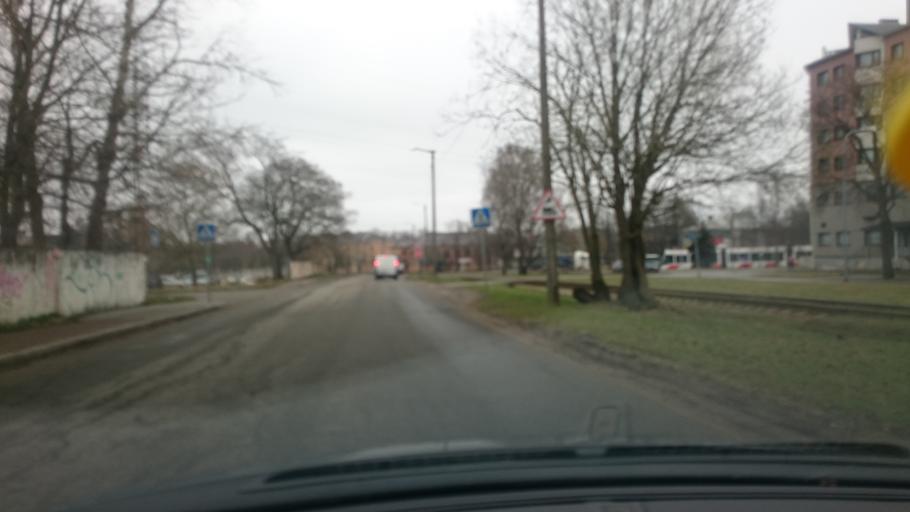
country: EE
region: Harju
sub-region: Tallinna linn
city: Tallinn
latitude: 59.4561
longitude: 24.6888
